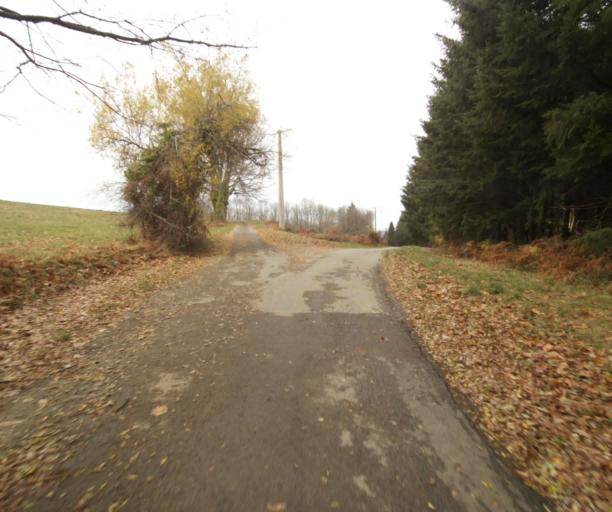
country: FR
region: Limousin
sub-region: Departement de la Correze
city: Sainte-Fortunade
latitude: 45.1927
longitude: 1.7668
